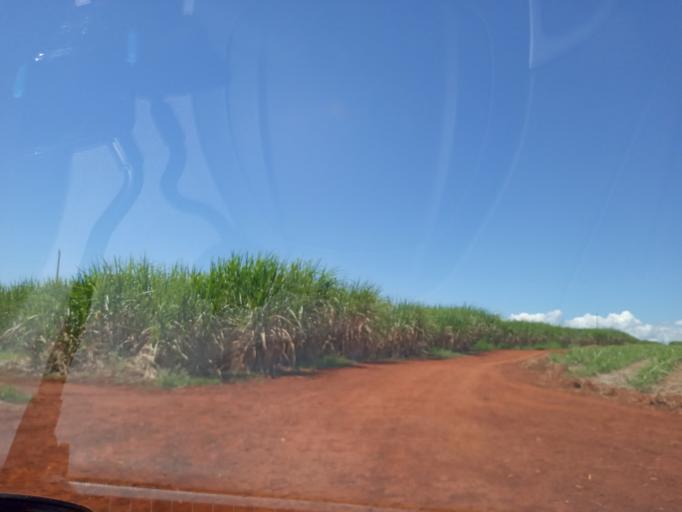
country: BR
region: Goias
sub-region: Itumbiara
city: Itumbiara
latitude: -18.4036
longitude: -49.1293
